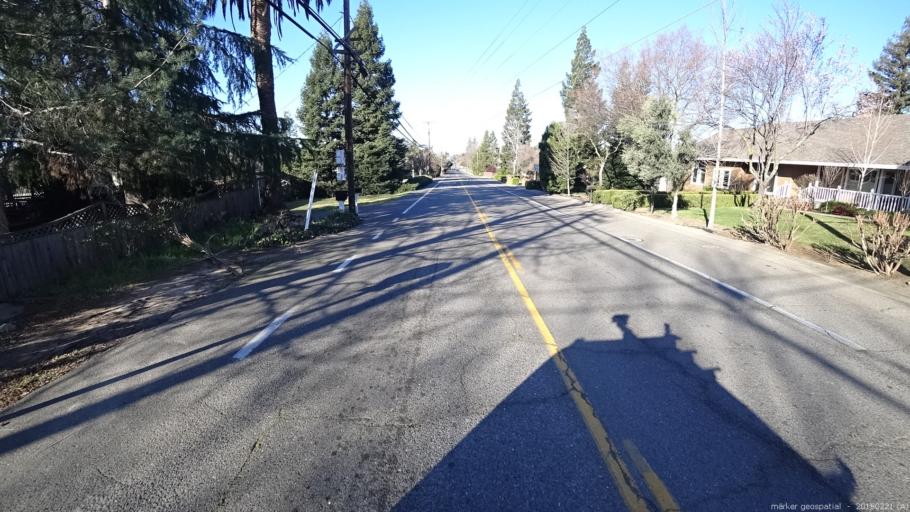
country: US
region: California
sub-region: Sacramento County
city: Orangevale
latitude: 38.6856
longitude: -121.2163
